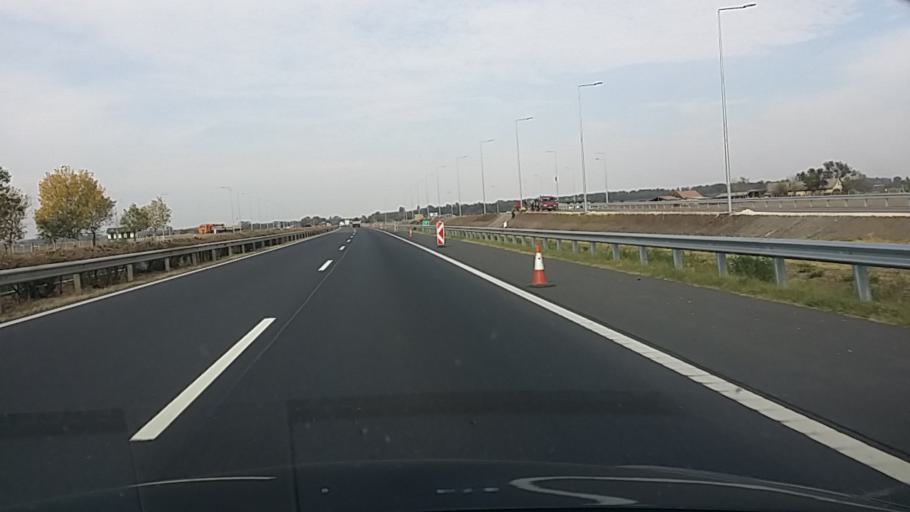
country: HU
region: Bacs-Kiskun
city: Lajosmizse
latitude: 46.9603
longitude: 19.6183
